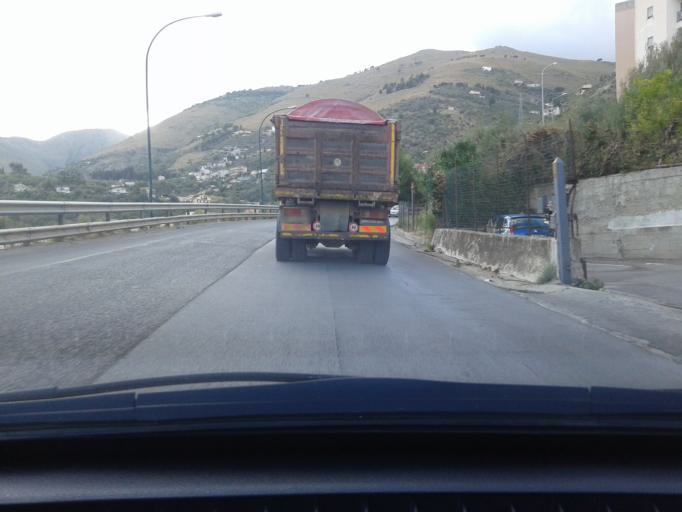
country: IT
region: Sicily
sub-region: Palermo
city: Monreale
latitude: 38.0744
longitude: 13.2839
